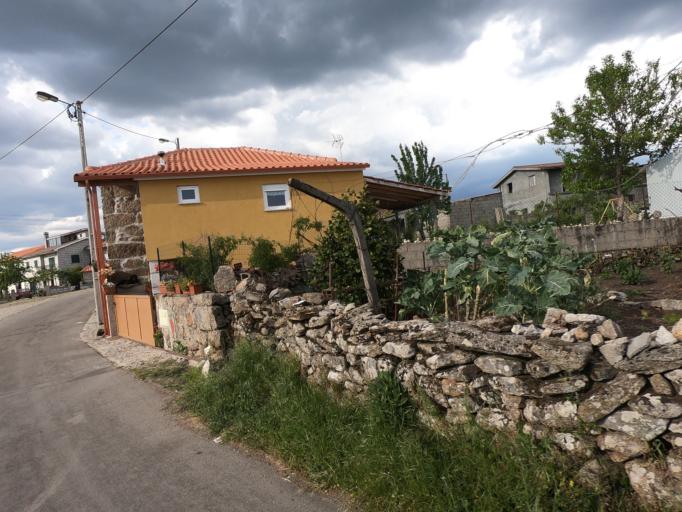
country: PT
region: Vila Real
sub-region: Vila Real
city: Vila Real
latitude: 41.3015
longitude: -7.6885
